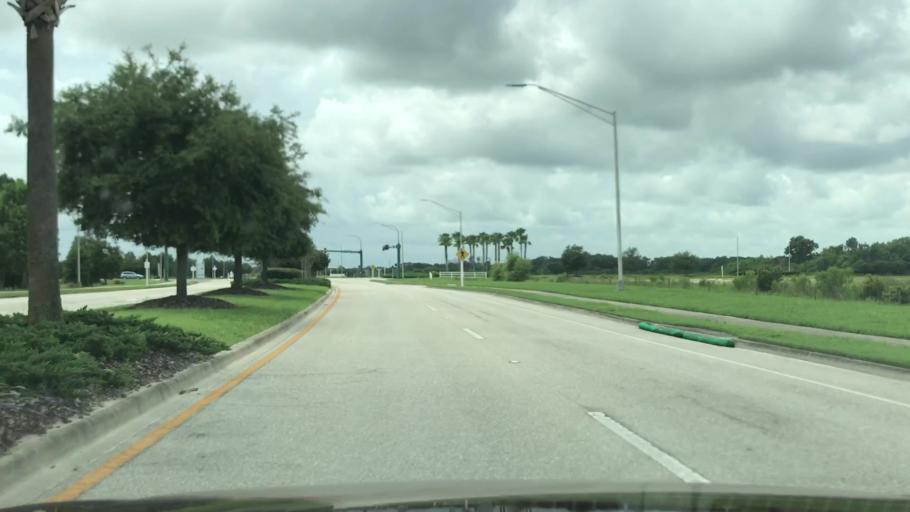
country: US
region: Florida
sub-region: Sarasota County
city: The Meadows
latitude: 27.4441
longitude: -82.4152
